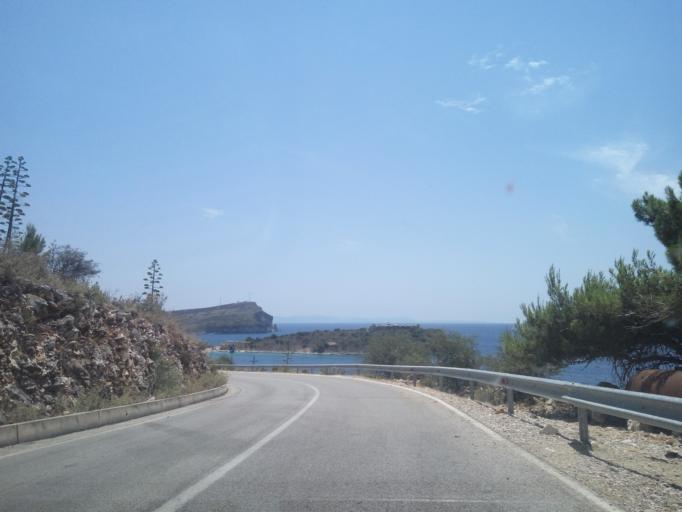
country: AL
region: Vlore
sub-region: Rrethi i Vlores
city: Himare
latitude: 40.0681
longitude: 19.7921
